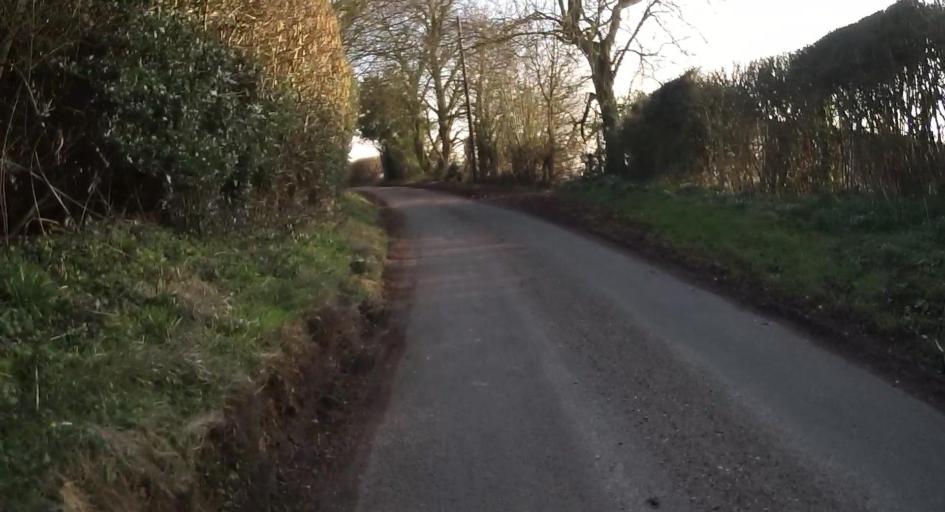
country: GB
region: England
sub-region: Hampshire
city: Alton
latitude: 51.1681
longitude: -1.0020
